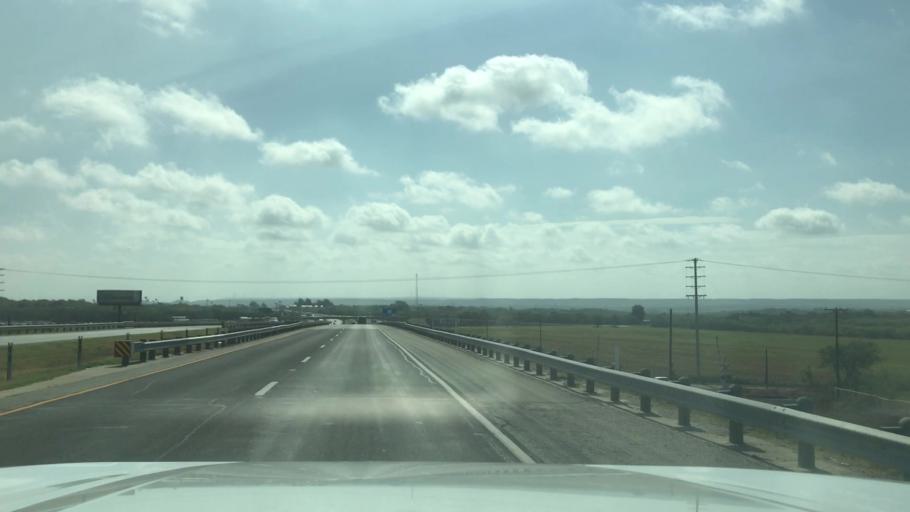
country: US
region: Texas
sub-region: Nolan County
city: Sweetwater
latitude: 32.4477
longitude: -100.4212
